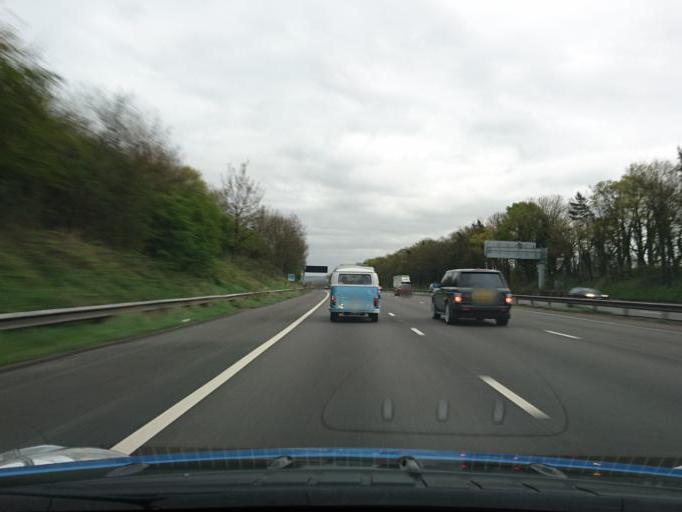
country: GB
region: England
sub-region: Staffordshire
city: Stafford
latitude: 52.7885
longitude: -2.1413
